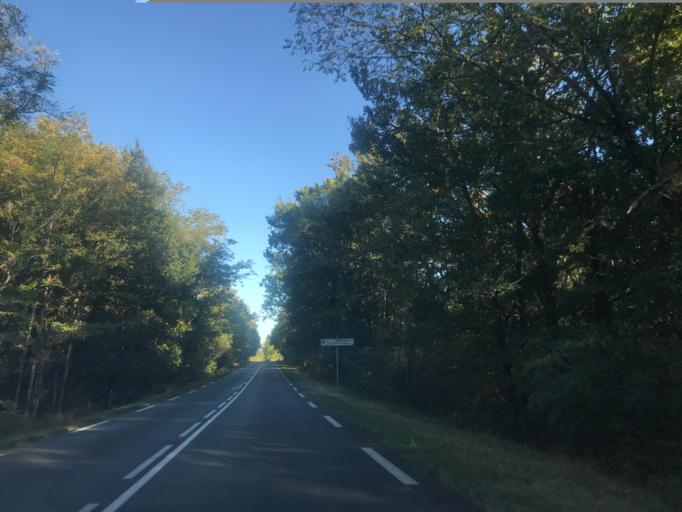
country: FR
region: Poitou-Charentes
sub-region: Departement de la Charente-Maritime
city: Saint-Aigulin
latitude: 45.1669
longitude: -0.0421
